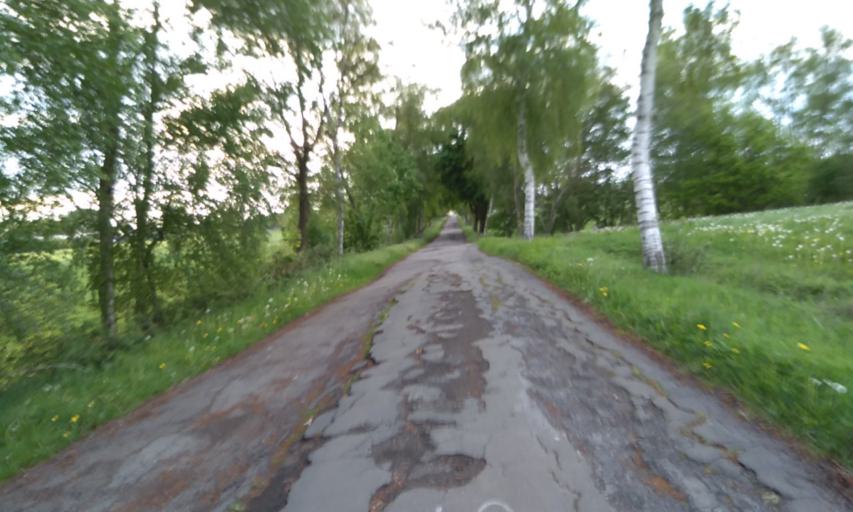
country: DE
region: Lower Saxony
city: Ahlerstedt
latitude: 53.3938
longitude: 9.4949
